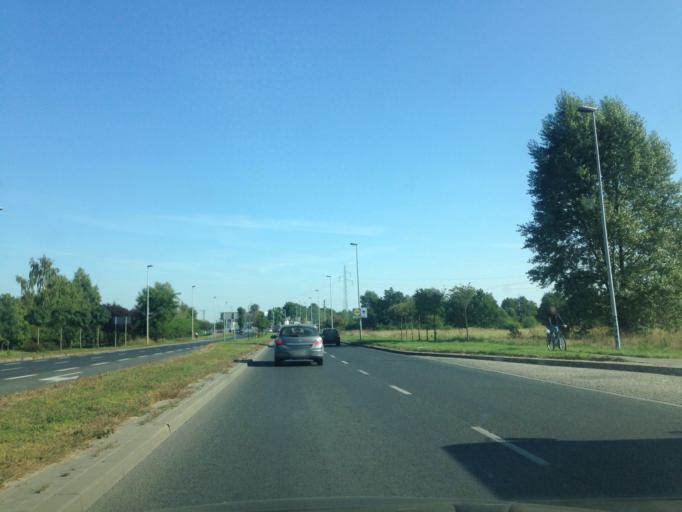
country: PL
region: Kujawsko-Pomorskie
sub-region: Powiat torunski
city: Lubicz Dolny
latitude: 53.0358
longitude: 18.6865
